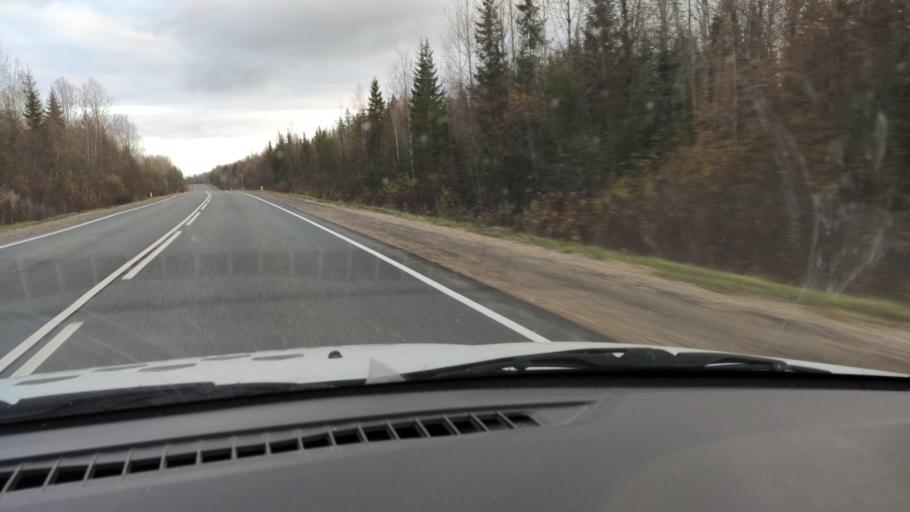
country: RU
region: Kirov
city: Omutninsk
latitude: 58.7077
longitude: 52.1016
